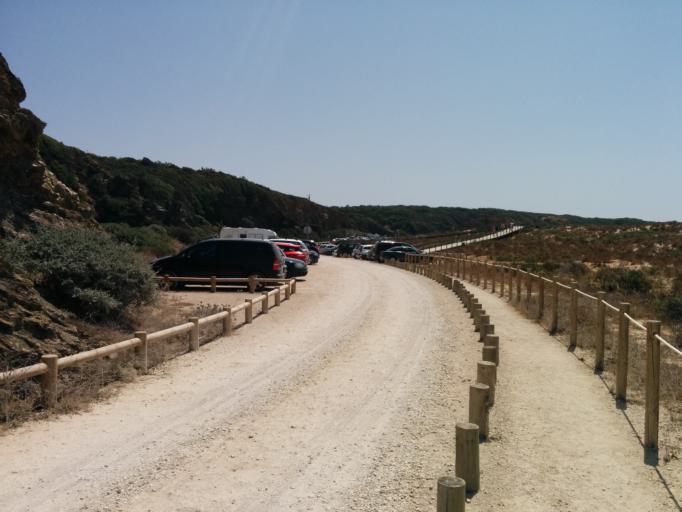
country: PT
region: Beja
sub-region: Odemira
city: Vila Nova de Milfontes
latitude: 37.7173
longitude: -8.7841
